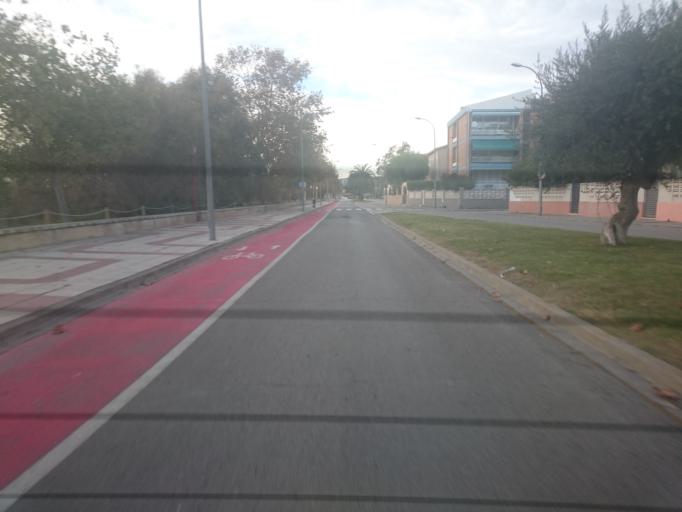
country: ES
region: Catalonia
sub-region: Provincia de Barcelona
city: Cubelles
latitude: 41.2007
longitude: 1.6756
